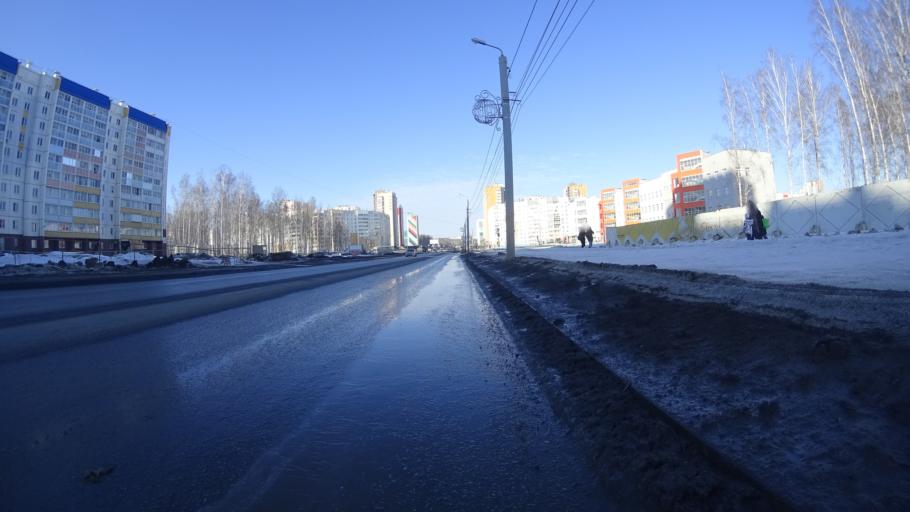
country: RU
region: Chelyabinsk
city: Roshchino
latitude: 55.2046
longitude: 61.2844
